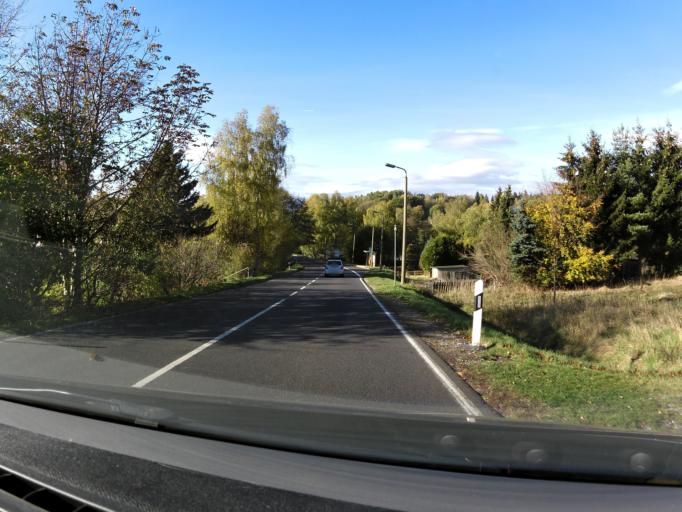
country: DE
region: Thuringia
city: Martinroda
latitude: 50.6976
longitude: 10.8934
